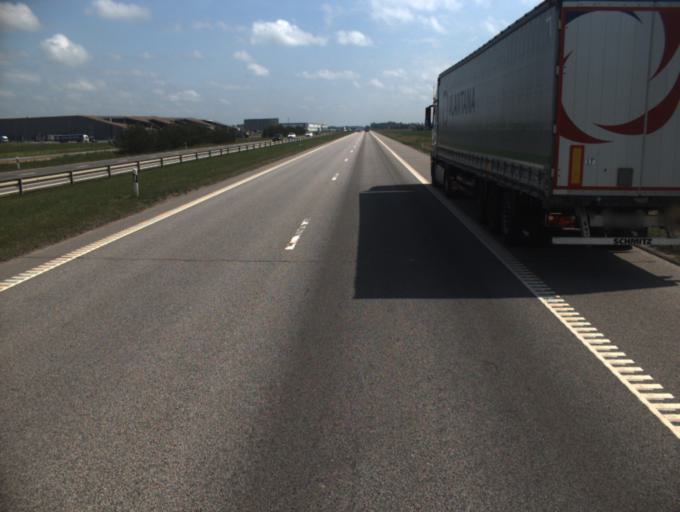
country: LT
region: Klaipedos apskritis
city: Gargzdai
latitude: 55.7124
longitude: 21.2671
